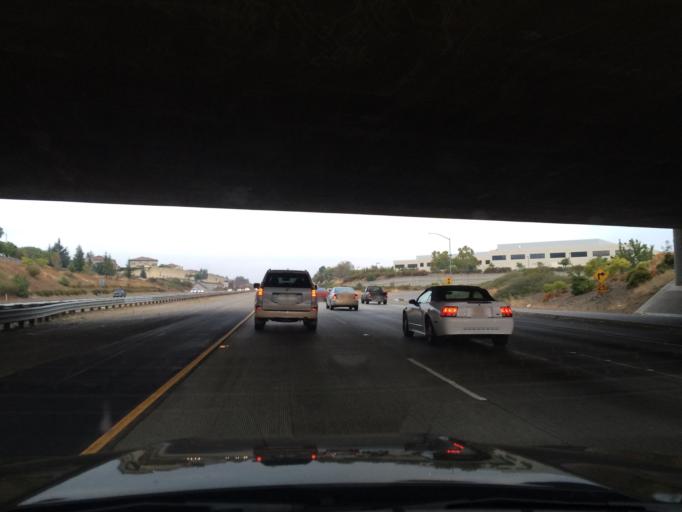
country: US
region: California
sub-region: Santa Clara County
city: Cambrian Park
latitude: 37.2510
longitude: -121.9312
